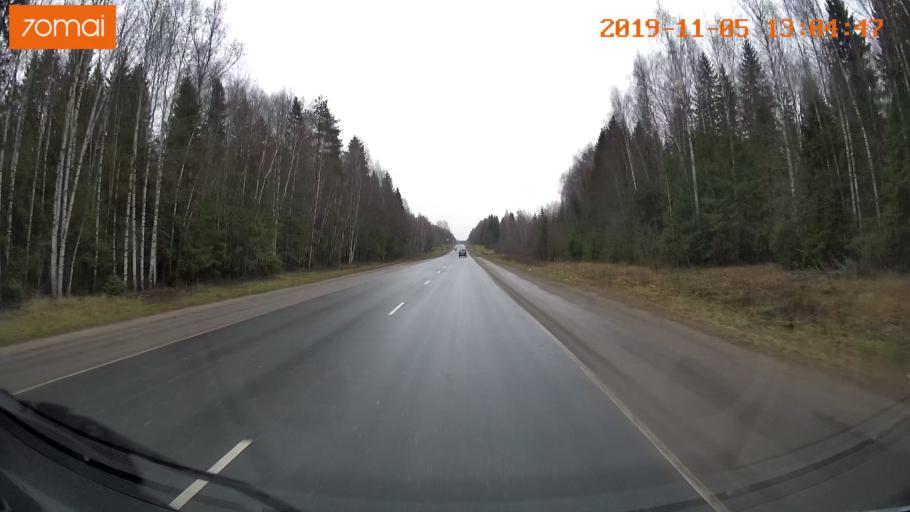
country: RU
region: Ivanovo
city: Kitovo
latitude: 56.8868
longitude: 41.2285
